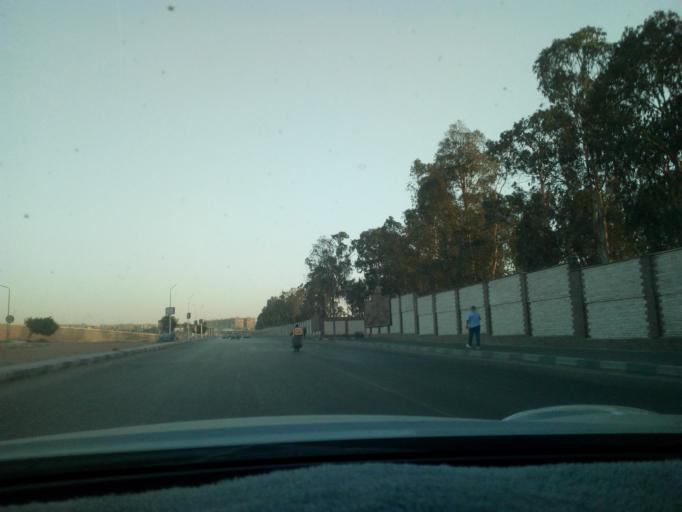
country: EG
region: Muhafazat al Qalyubiyah
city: Al Khankah
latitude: 30.1162
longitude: 31.3646
